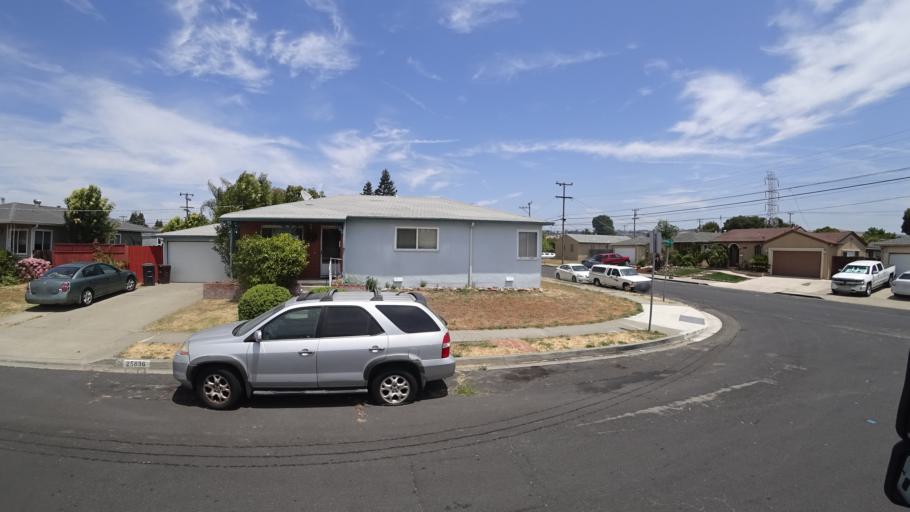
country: US
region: California
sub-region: Alameda County
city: Hayward
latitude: 37.6453
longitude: -122.0895
